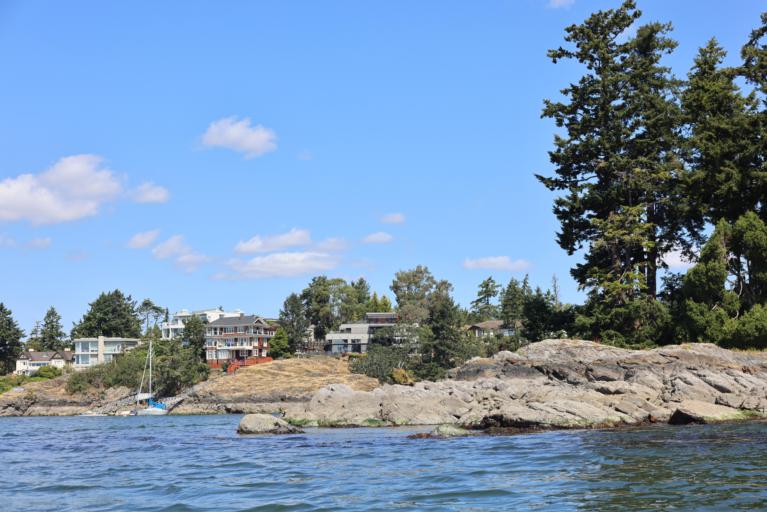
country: CA
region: British Columbia
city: Colwood
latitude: 48.4506
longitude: -123.4436
